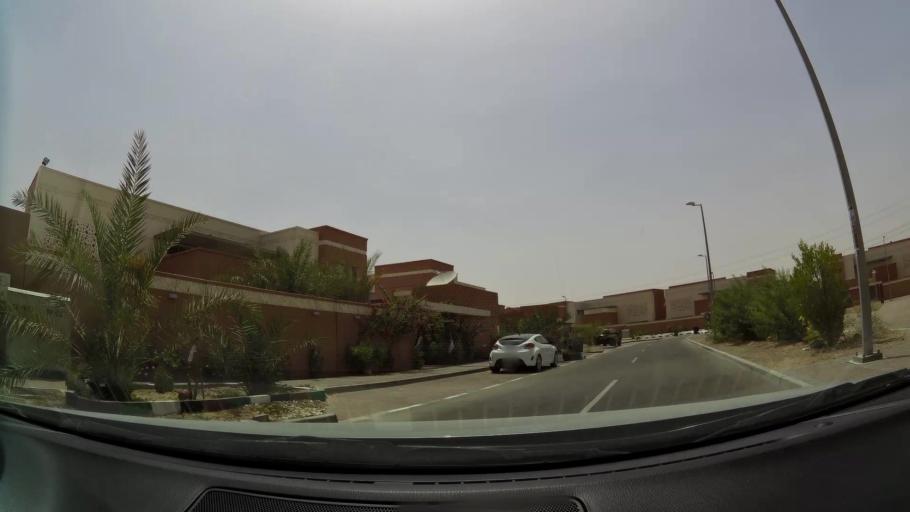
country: AE
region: Abu Dhabi
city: Al Ain
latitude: 24.1435
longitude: 55.6172
